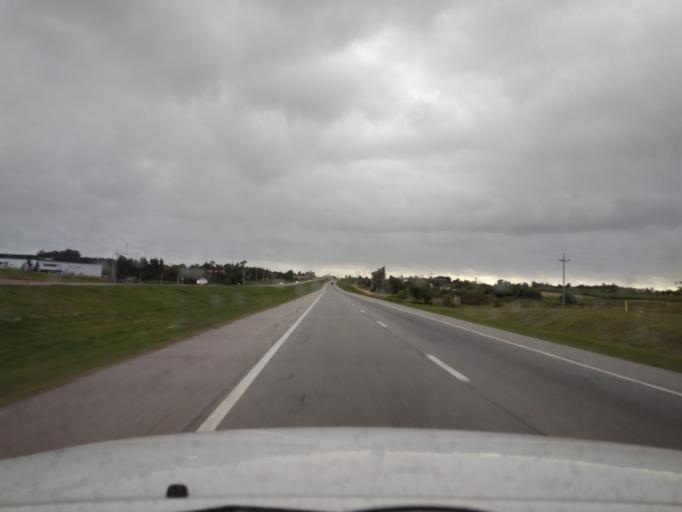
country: UY
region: Canelones
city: Las Piedras
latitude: -34.7080
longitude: -56.2420
